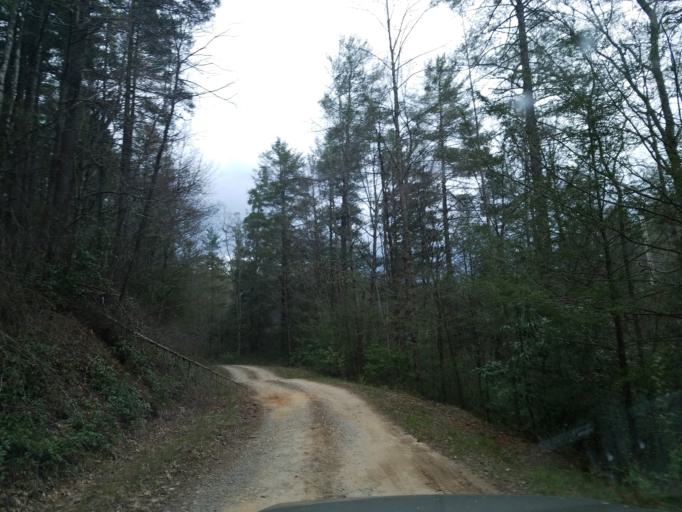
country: US
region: Georgia
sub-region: Union County
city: Blairsville
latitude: 34.7726
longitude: -84.0940
